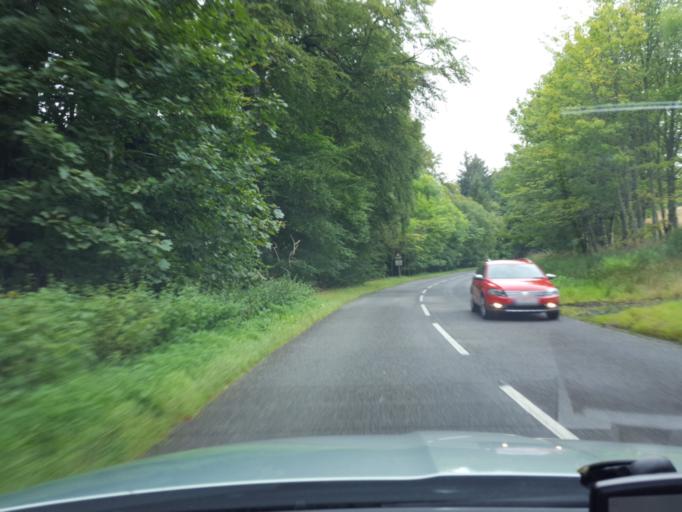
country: GB
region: Scotland
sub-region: Aberdeenshire
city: Banchory
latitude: 57.1414
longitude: -2.4902
